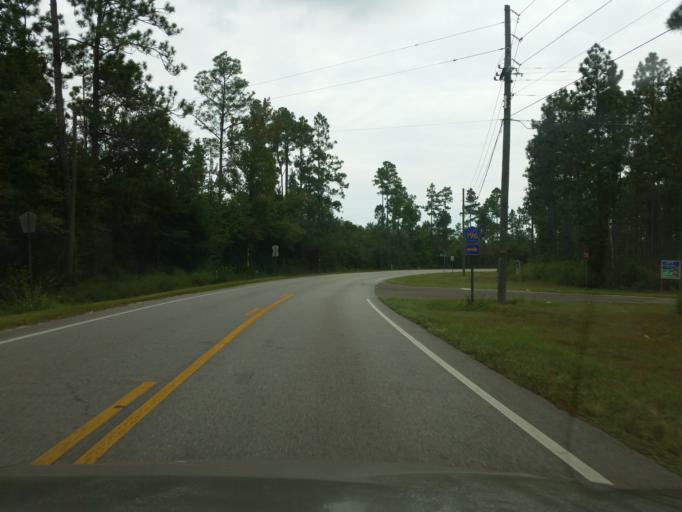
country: US
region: Florida
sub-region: Escambia County
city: Molino
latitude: 30.6786
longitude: -87.3196
